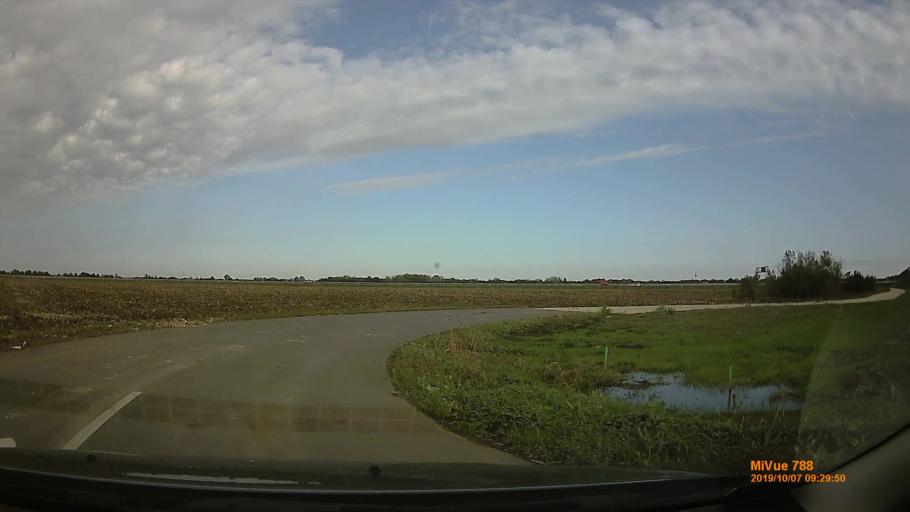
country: HU
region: Bekes
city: Szarvas
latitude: 46.8115
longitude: 20.6471
